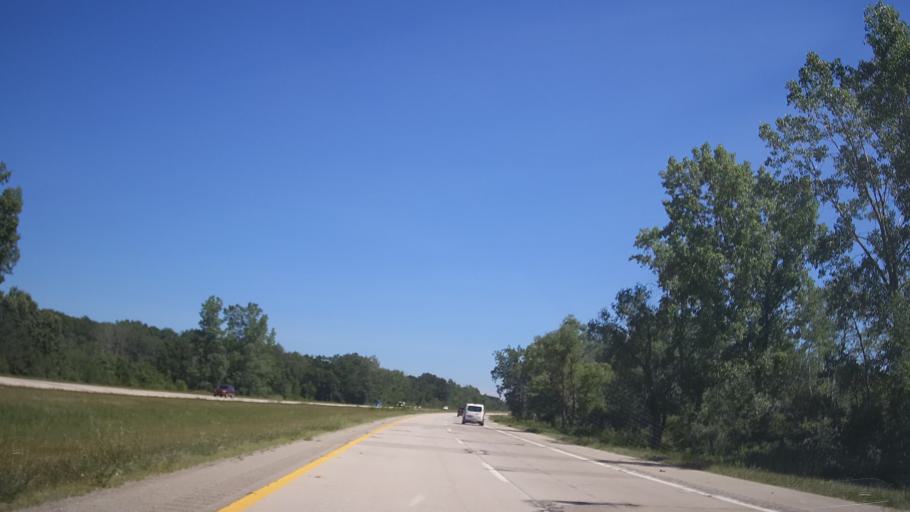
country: US
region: Michigan
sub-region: Midland County
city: Coleman
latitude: 43.7795
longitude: -84.6177
